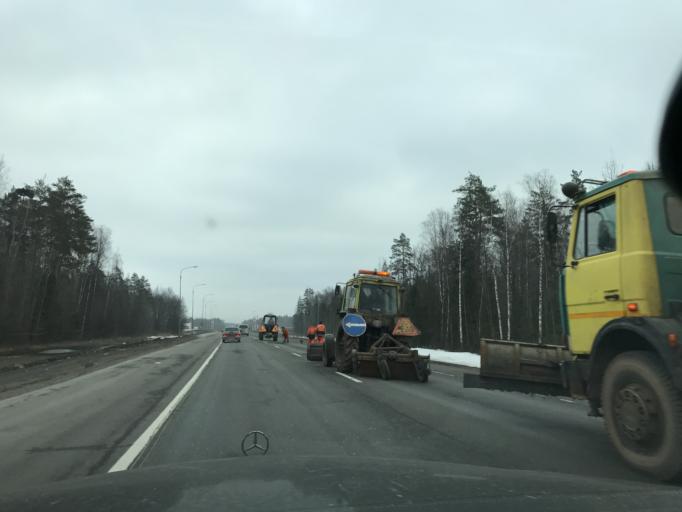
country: RU
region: Vladimir
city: Raduzhnyy
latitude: 56.0715
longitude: 40.2313
